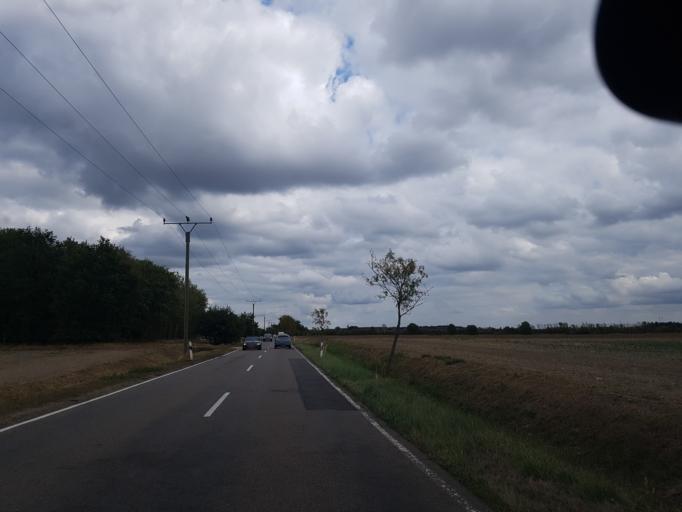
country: DE
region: Saxony-Anhalt
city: Klieken
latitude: 51.9297
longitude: 12.3653
